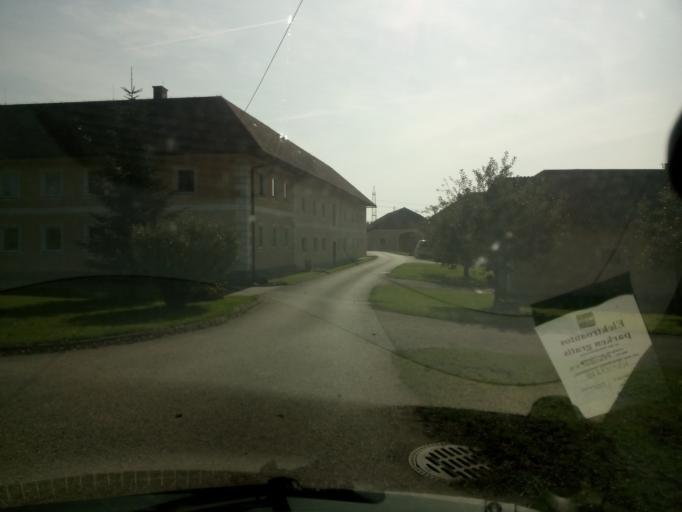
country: AT
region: Upper Austria
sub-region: Wels-Land
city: Steinhaus
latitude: 48.0881
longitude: 14.0277
